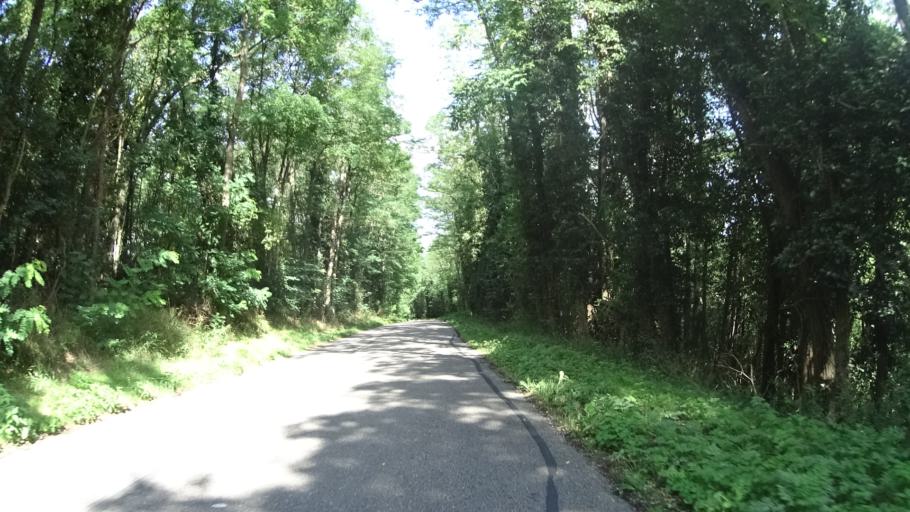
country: FR
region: Lorraine
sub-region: Departement de Meurthe-et-Moselle
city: Dommartin-les-Toul
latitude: 48.6471
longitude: 5.9193
